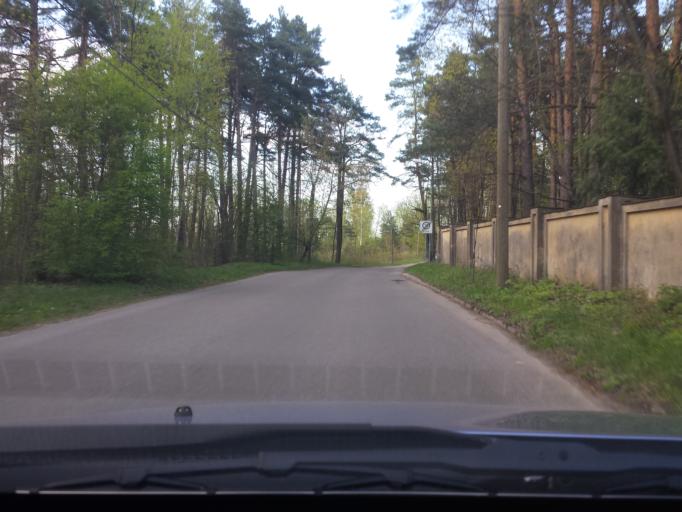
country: LV
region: Riga
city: Jaunciems
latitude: 56.9899
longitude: 24.2073
